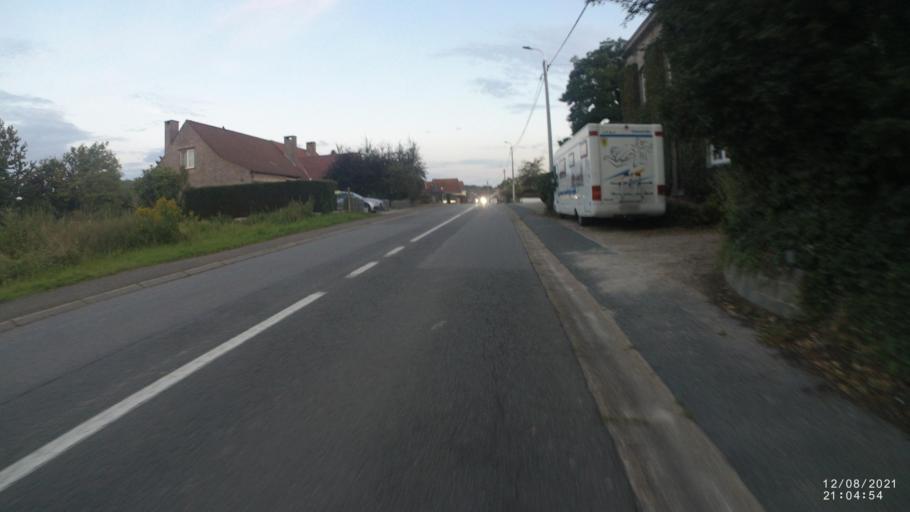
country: BE
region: Flanders
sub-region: Provincie Vlaams-Brabant
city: Dilbeek
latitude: 50.8566
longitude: 4.2474
